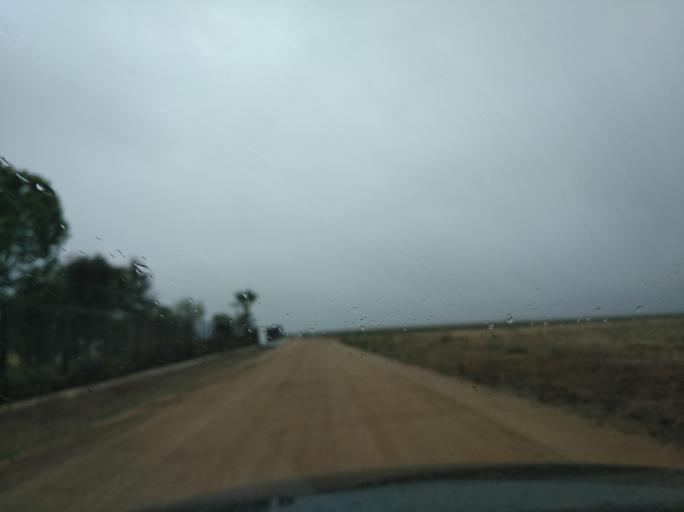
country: PT
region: Portalegre
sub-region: Campo Maior
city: Campo Maior
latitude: 38.9495
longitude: -7.0692
